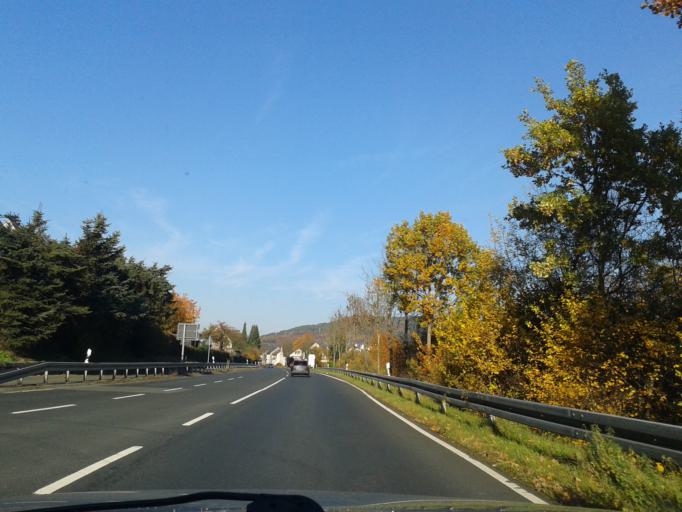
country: DE
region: Hesse
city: Dillenburg
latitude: 50.8069
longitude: 8.3377
